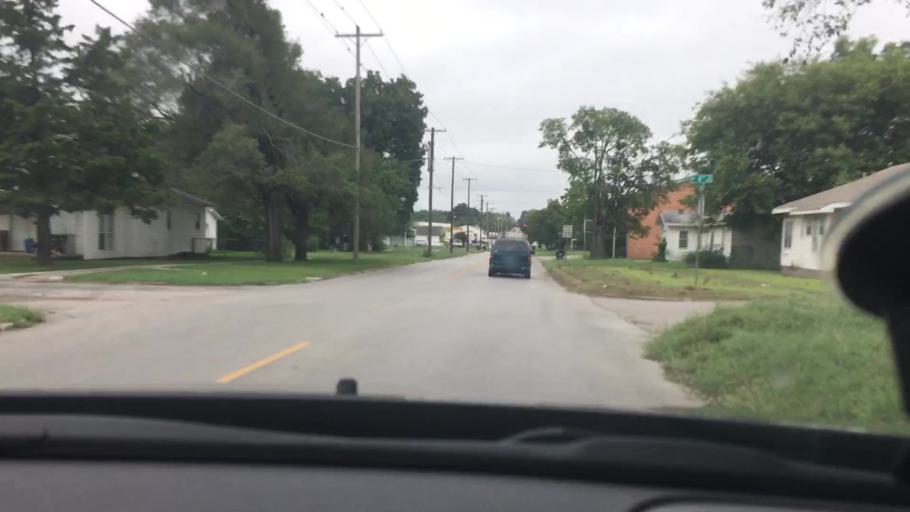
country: US
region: Oklahoma
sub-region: Pontotoc County
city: Ada
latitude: 34.7779
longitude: -96.6867
